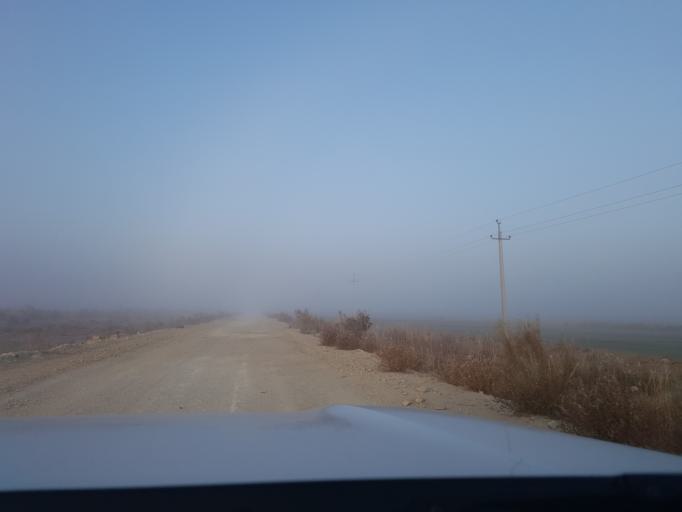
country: TM
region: Dasoguz
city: Koeneuergench
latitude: 41.8455
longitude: 58.4205
